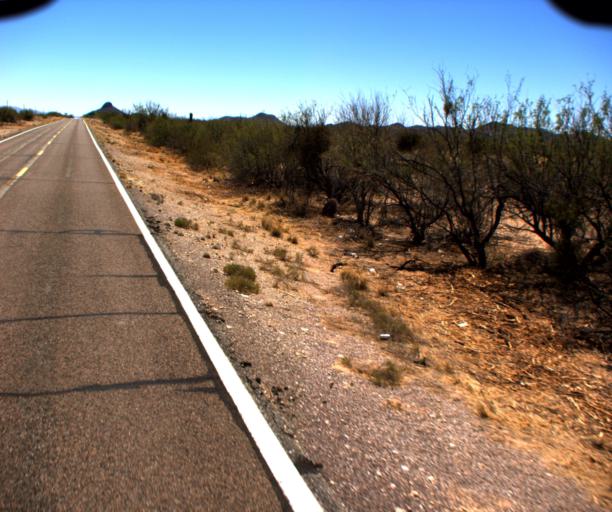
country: US
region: Arizona
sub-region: Pima County
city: Ajo
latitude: 32.2065
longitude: -112.5756
